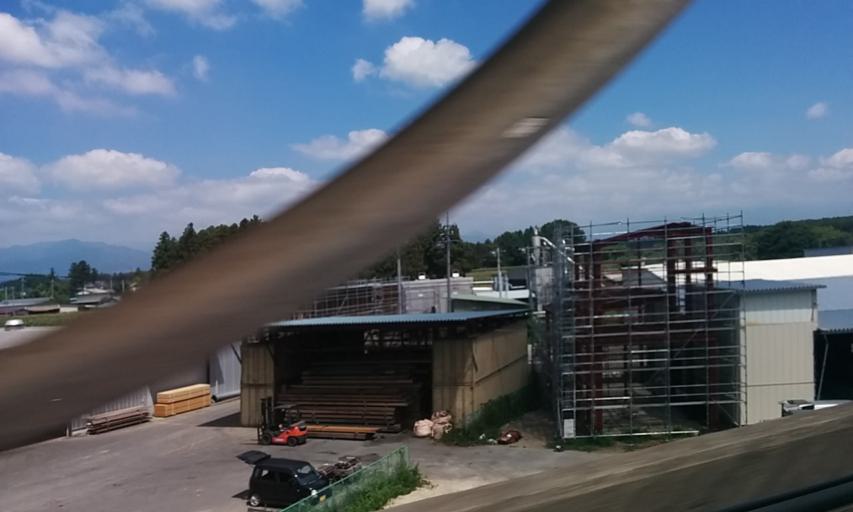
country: JP
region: Tochigi
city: Otawara
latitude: 36.9097
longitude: 140.0046
